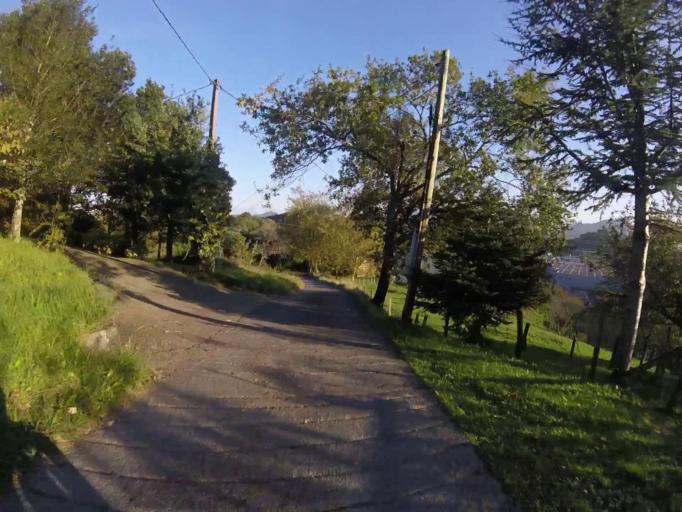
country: ES
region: Basque Country
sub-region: Provincia de Guipuzcoa
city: Lasarte
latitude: 43.2847
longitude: -2.0113
